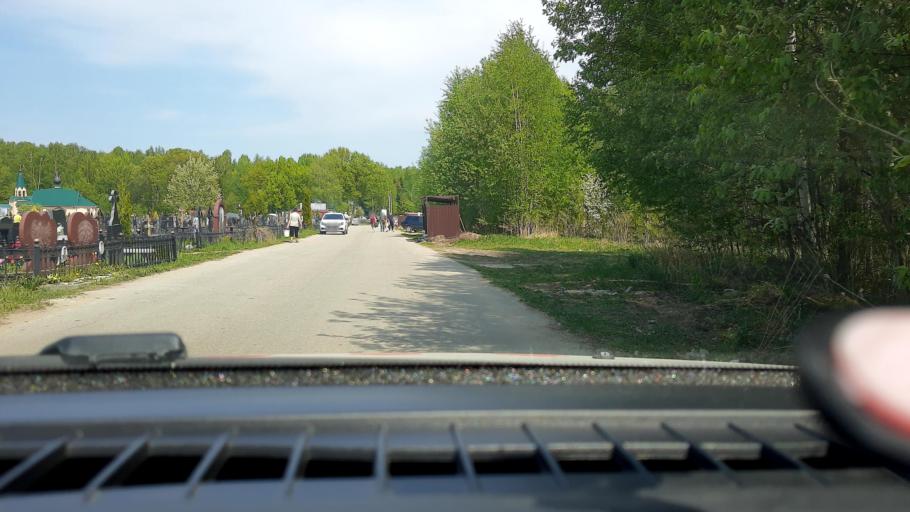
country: RU
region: Nizjnij Novgorod
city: Gorbatovka
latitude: 56.2300
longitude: 43.7611
